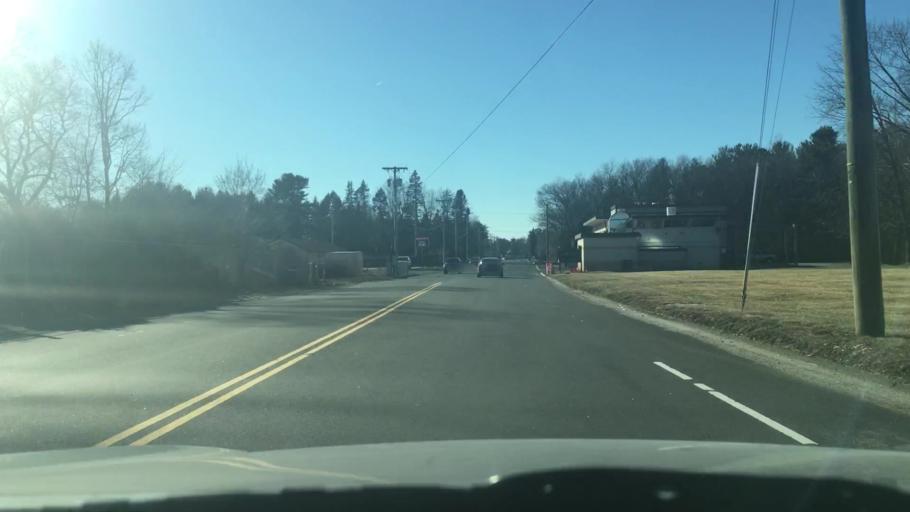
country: US
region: Massachusetts
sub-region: Hampden County
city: Ludlow
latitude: 42.1808
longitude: -72.5146
